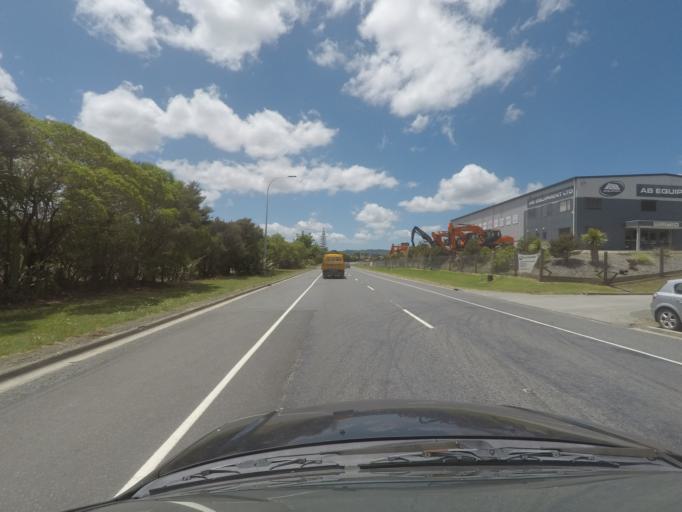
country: NZ
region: Northland
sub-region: Whangarei
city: Whangarei
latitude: -35.7455
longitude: 174.3233
